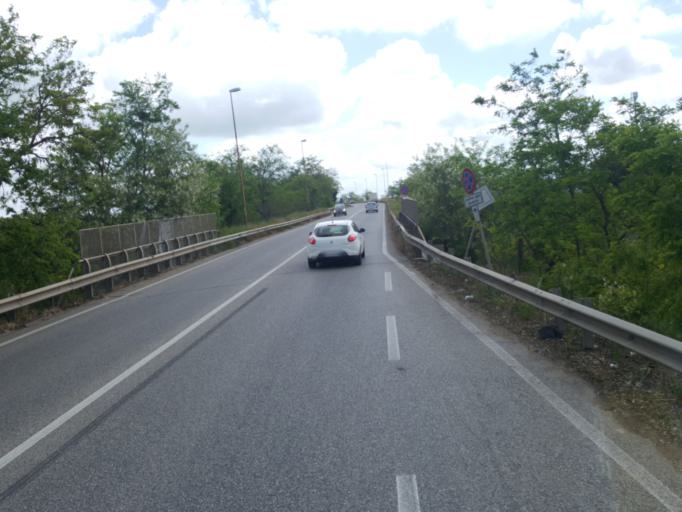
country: IT
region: Apulia
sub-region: Provincia di Bari
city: Altamura
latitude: 40.8154
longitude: 16.5535
